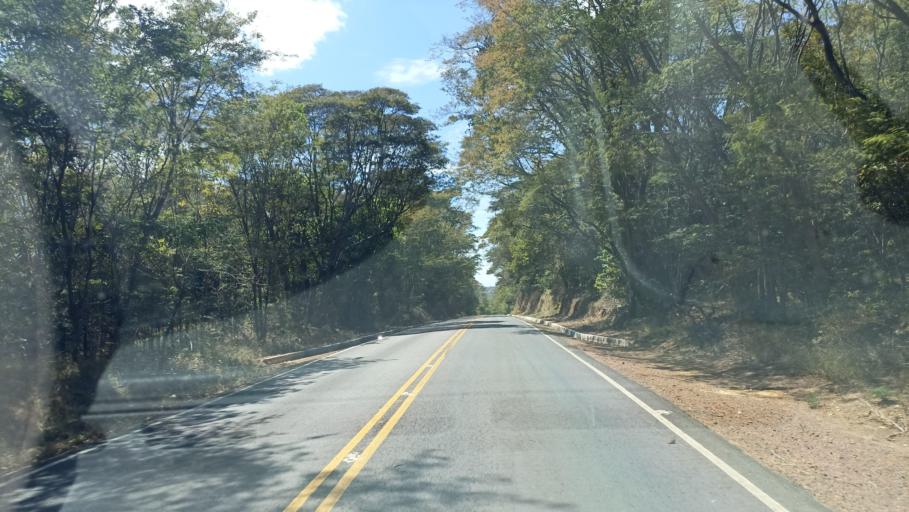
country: BR
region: Bahia
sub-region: Andarai
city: Vera Cruz
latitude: -12.7673
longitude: -41.3284
